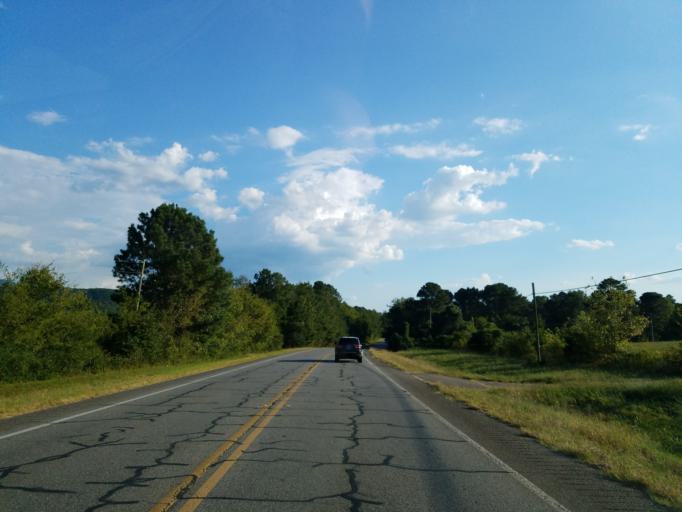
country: US
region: Georgia
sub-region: Murray County
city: Chatsworth
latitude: 34.9211
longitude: -84.7466
